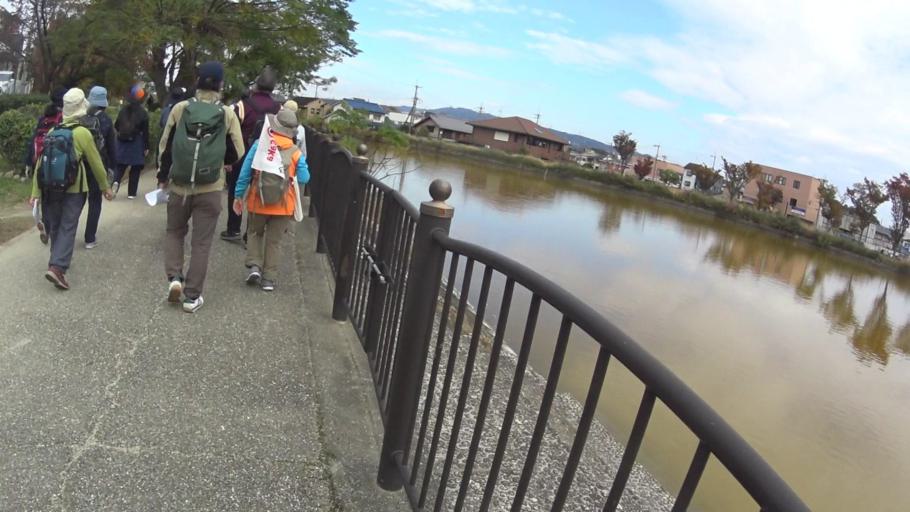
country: JP
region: Osaka
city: Kashihara
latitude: 34.5563
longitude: 135.5975
